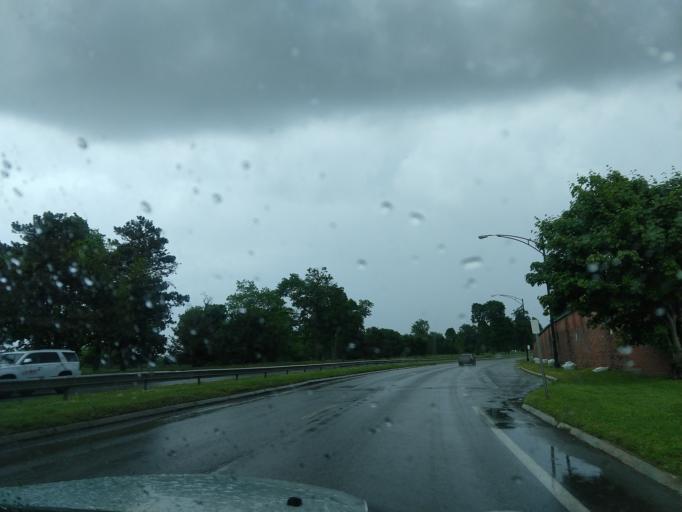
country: US
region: New York
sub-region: Erie County
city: Kenmore
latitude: 42.9333
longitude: -78.8594
